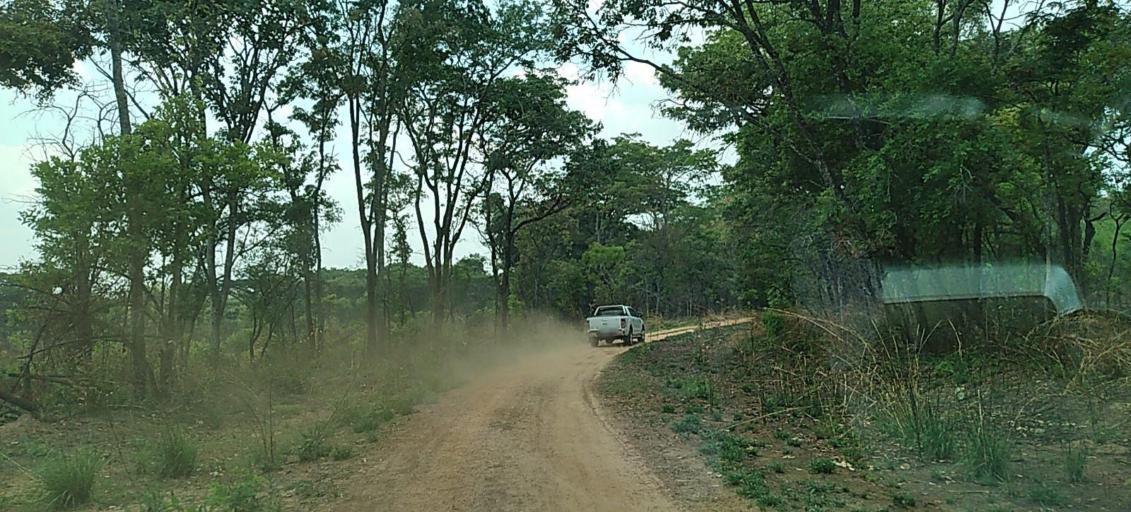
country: ZM
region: Copperbelt
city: Chingola
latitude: -12.7923
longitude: 27.6438
